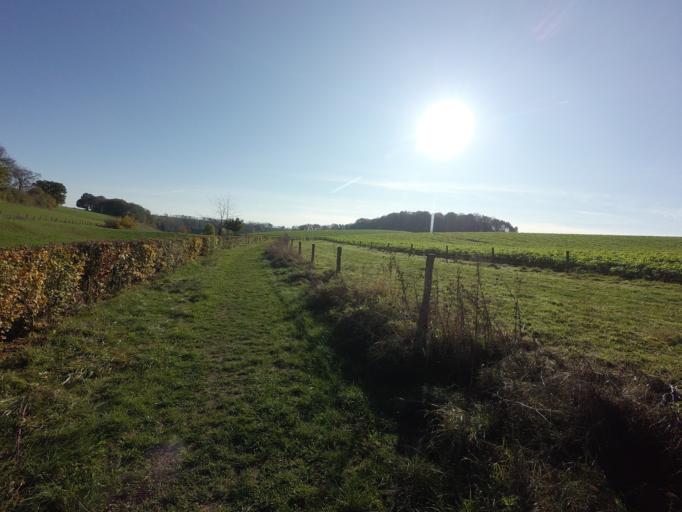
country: NL
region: Limburg
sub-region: Gemeente Voerendaal
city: Ubachsberg
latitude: 50.8323
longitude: 5.9534
